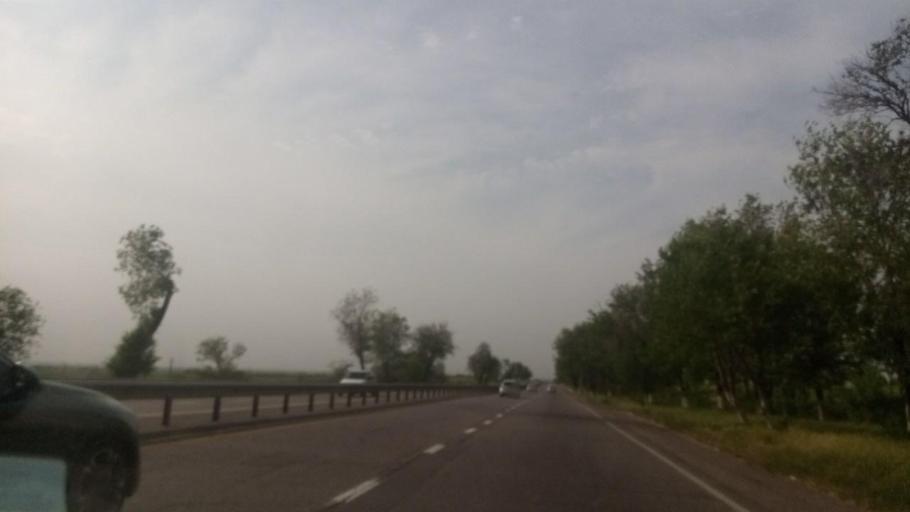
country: UZ
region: Toshkent
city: Tuytepa
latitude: 41.1032
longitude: 69.4542
